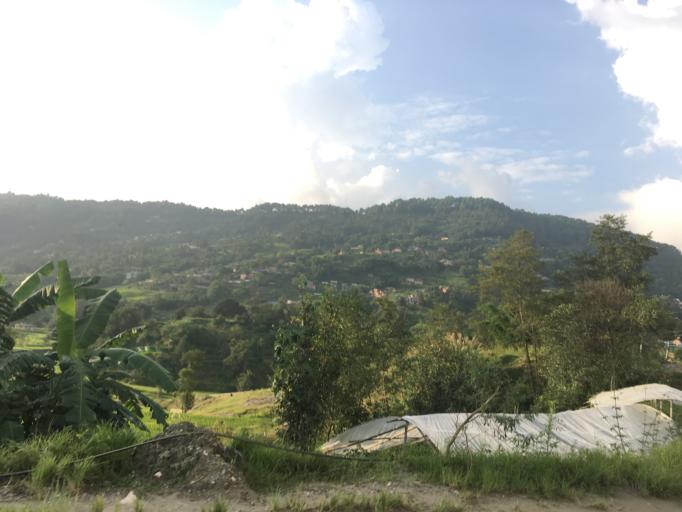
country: NP
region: Central Region
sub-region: Bagmati Zone
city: Bhaktapur
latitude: 27.6990
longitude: 85.4678
